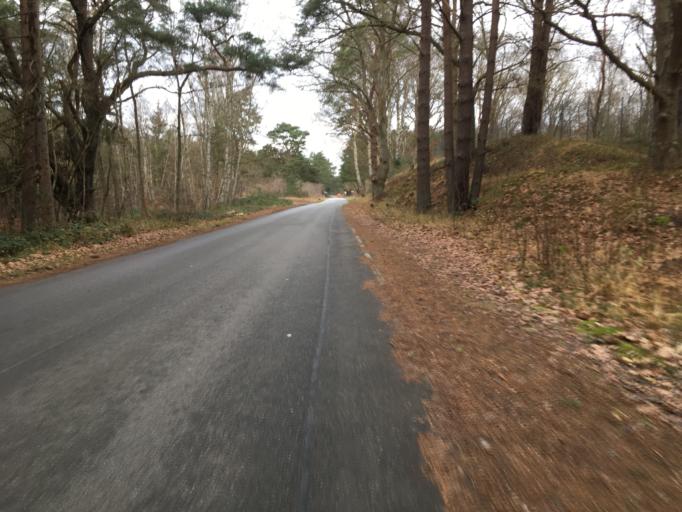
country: DE
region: Mecklenburg-Vorpommern
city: Ostseebad Binz
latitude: 54.4539
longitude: 13.5639
